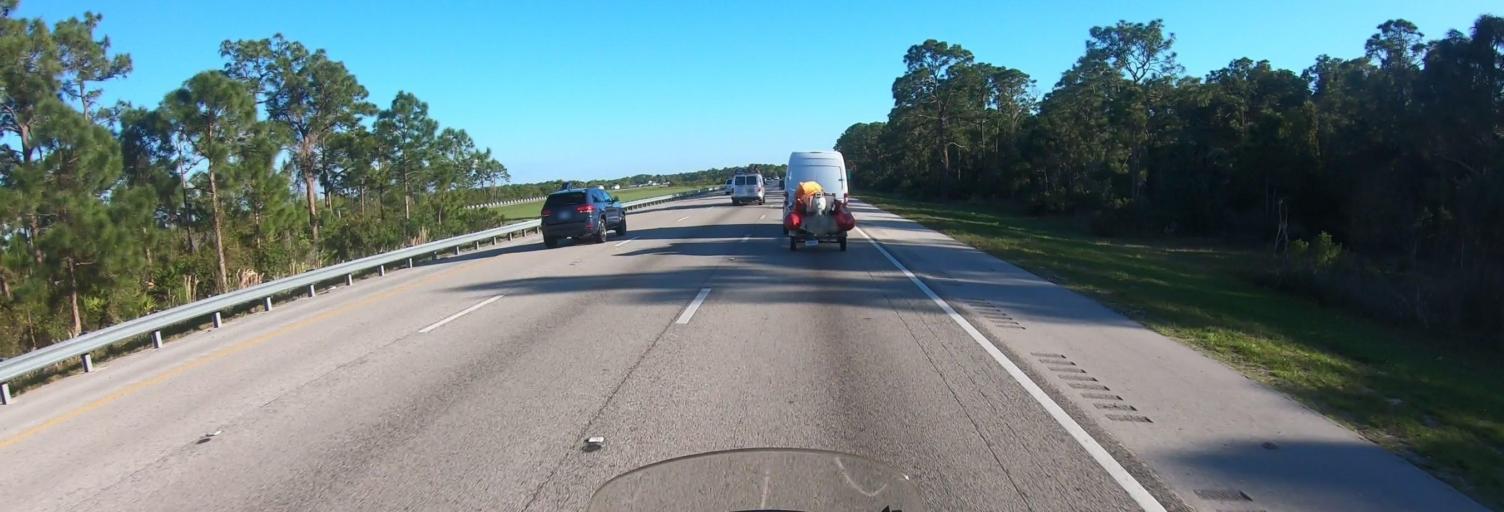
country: US
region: Florida
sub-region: Lee County
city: Suncoast Estates
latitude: 26.7635
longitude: -81.8769
